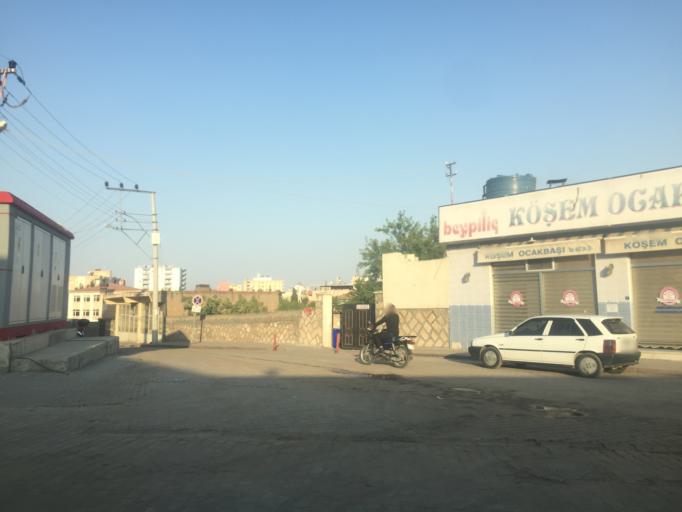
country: TR
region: Mardin
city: Midyat
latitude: 37.4267
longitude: 41.3394
